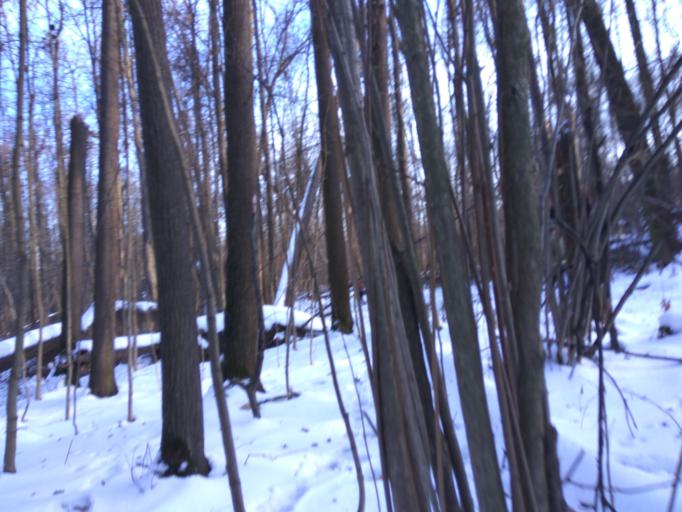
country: RU
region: Moscow
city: Babushkin
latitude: 55.8524
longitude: 37.7534
